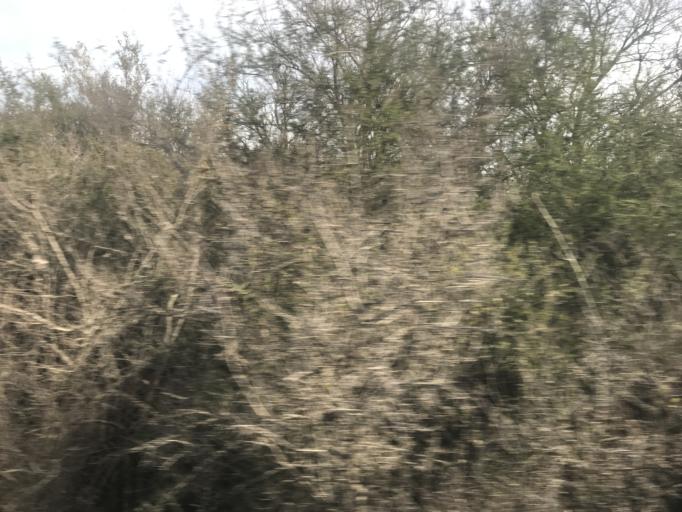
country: AR
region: Cordoba
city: Pilar
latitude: -31.7045
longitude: -63.8662
